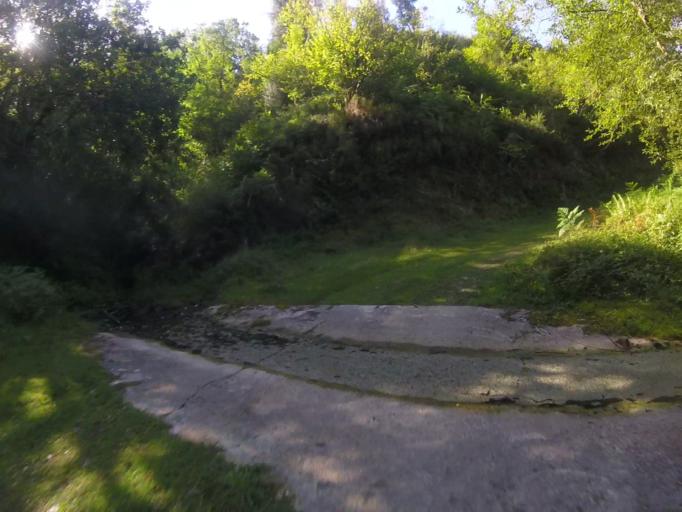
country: ES
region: Navarre
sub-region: Provincia de Navarra
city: Arano
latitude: 43.2288
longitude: -1.8653
